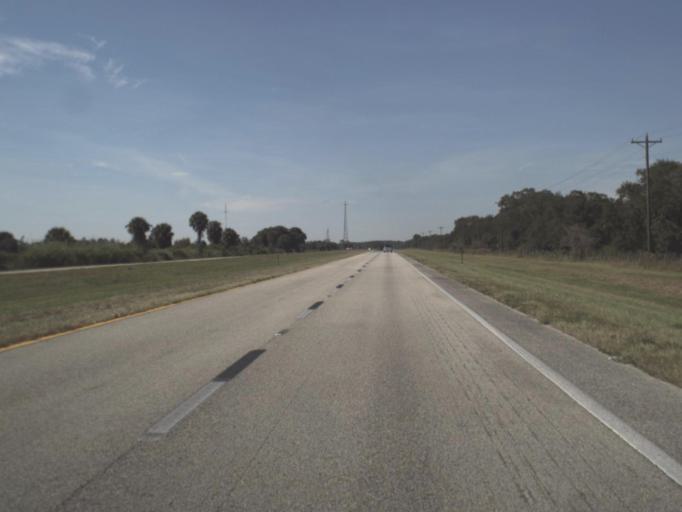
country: US
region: Florida
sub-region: Hendry County
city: Port LaBelle
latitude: 26.9202
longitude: -81.2989
